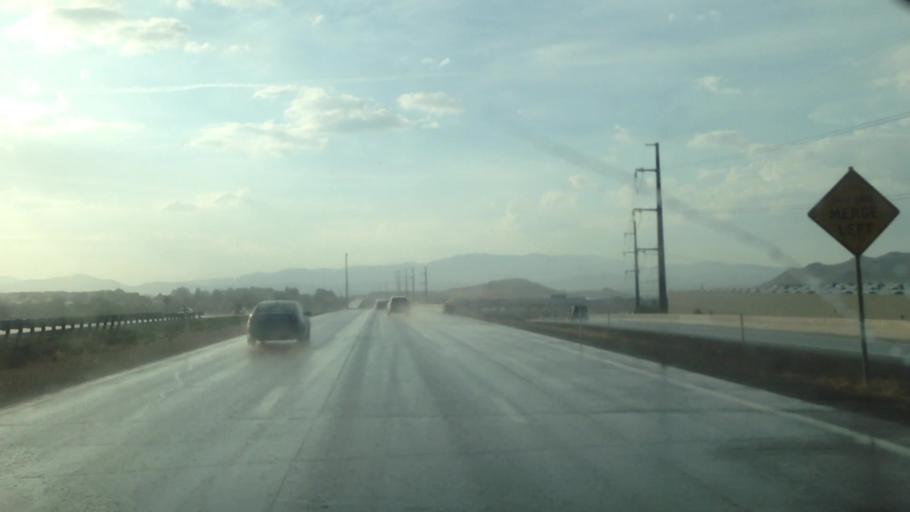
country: US
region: Nevada
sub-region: Washoe County
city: Golden Valley
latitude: 39.5971
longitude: -119.8335
